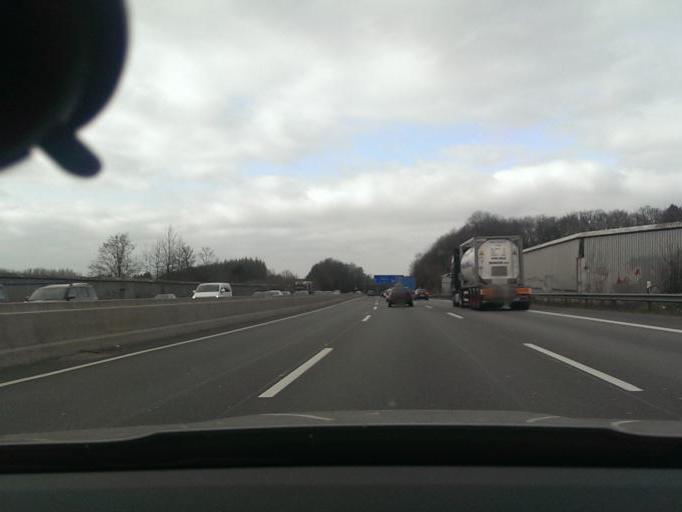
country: DE
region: North Rhine-Westphalia
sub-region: Regierungsbezirk Detmold
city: Oerlinghausen
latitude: 51.9823
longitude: 8.6159
